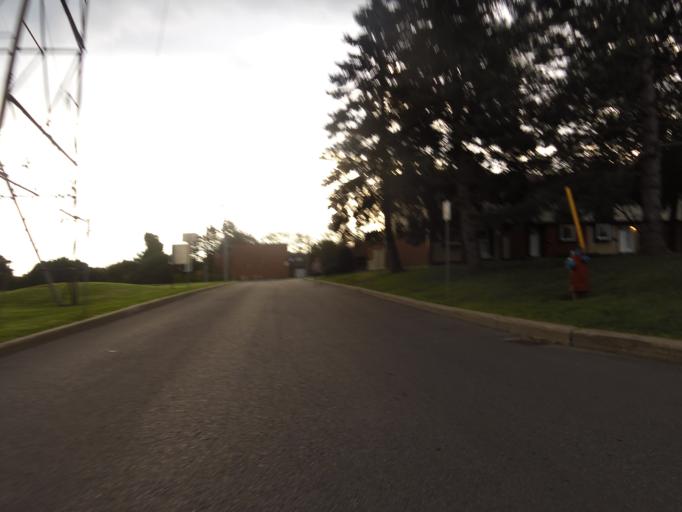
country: CA
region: Ontario
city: Bells Corners
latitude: 45.3183
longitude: -75.8280
